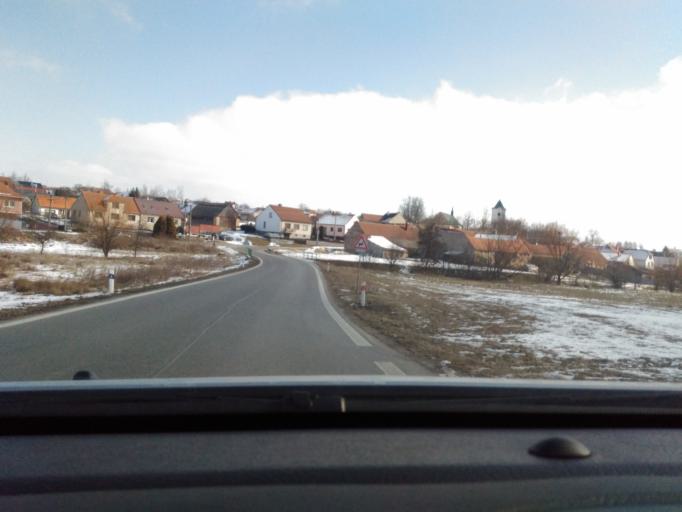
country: CZ
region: Vysocina
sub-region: Okres Zd'ar nad Sazavou
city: Velka Bites
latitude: 49.3241
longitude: 16.1632
